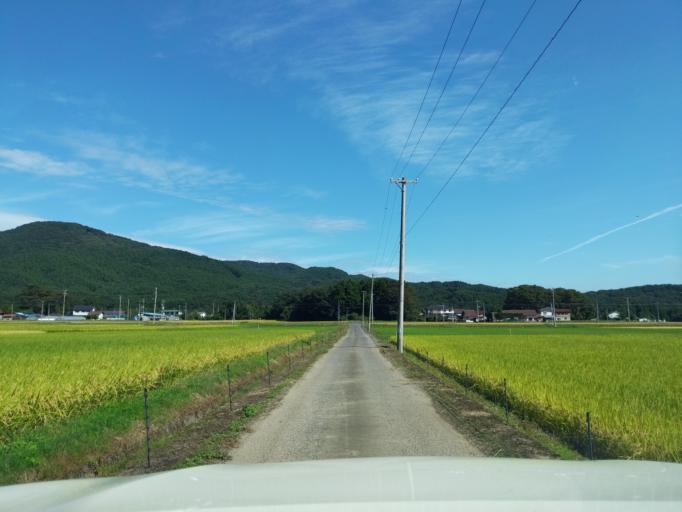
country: JP
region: Fukushima
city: Koriyama
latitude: 37.4066
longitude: 140.2399
